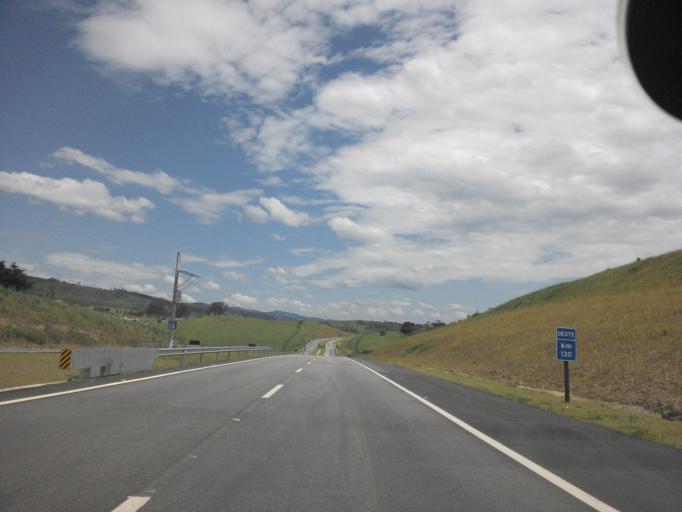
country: BR
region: Sao Paulo
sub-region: Taubate
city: Taubate
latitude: -23.0952
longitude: -45.5844
